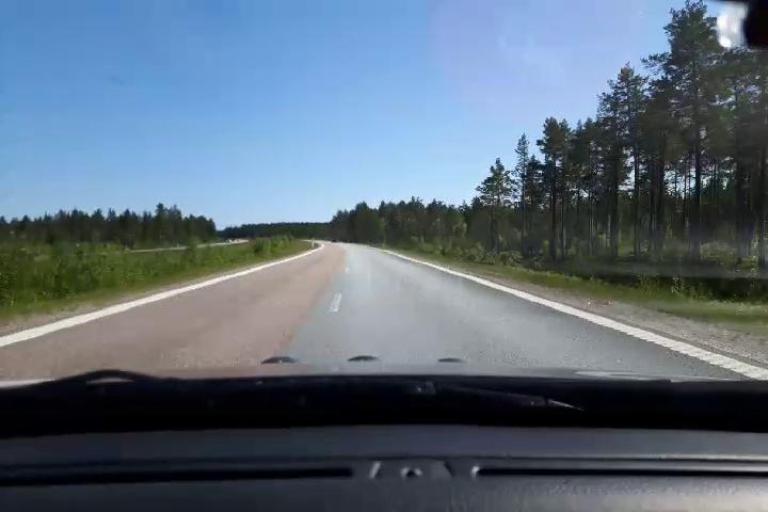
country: SE
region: Gaevleborg
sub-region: Soderhamns Kommun
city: Soderhamn
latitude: 61.3797
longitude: 16.9938
